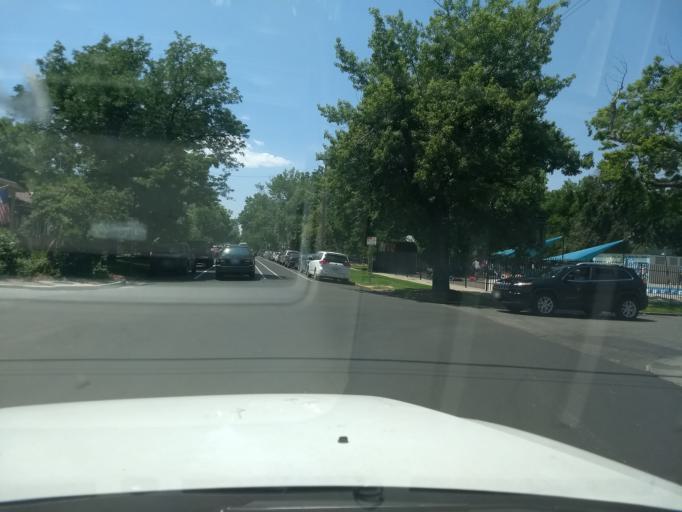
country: US
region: Colorado
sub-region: Denver County
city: Denver
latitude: 39.7615
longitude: -104.9745
